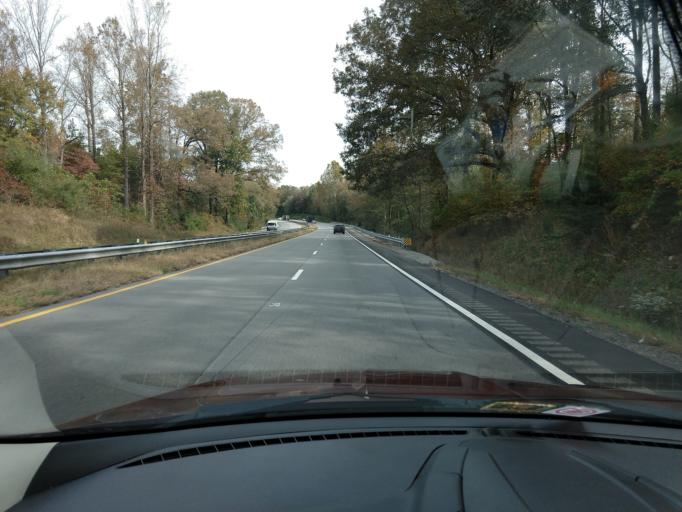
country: US
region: Virginia
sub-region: Pittsylvania County
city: Chatham
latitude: 36.8180
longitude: -79.3819
